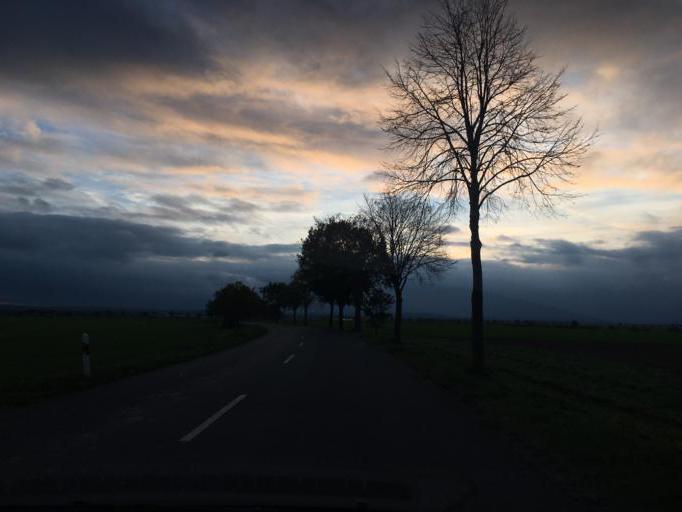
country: DE
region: North Rhine-Westphalia
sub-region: Regierungsbezirk Koln
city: Vettweiss
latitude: 50.7581
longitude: 6.6281
